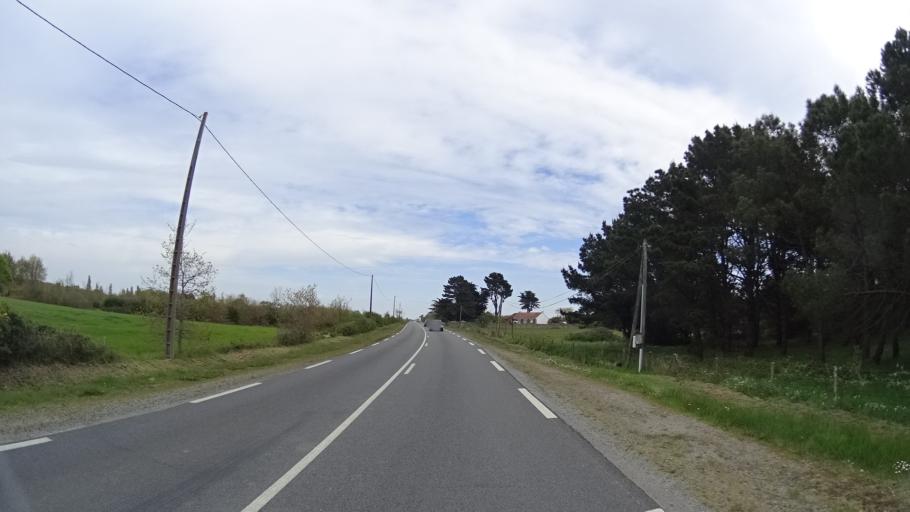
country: FR
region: Pays de la Loire
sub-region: Departement de la Loire-Atlantique
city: Bourgneuf-en-Retz
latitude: 47.0462
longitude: -1.9392
